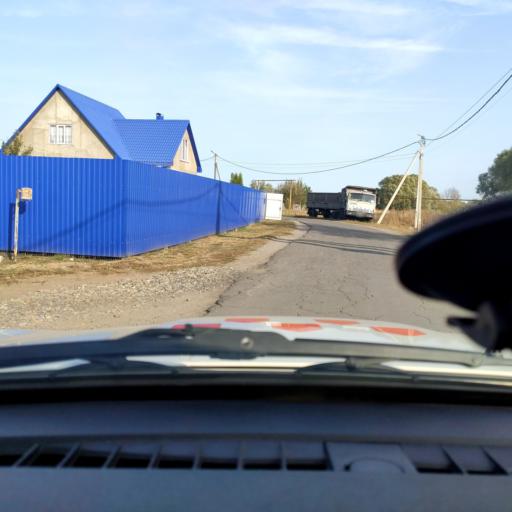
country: RU
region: Voronezj
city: Novaya Usman'
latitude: 51.6208
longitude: 39.4090
